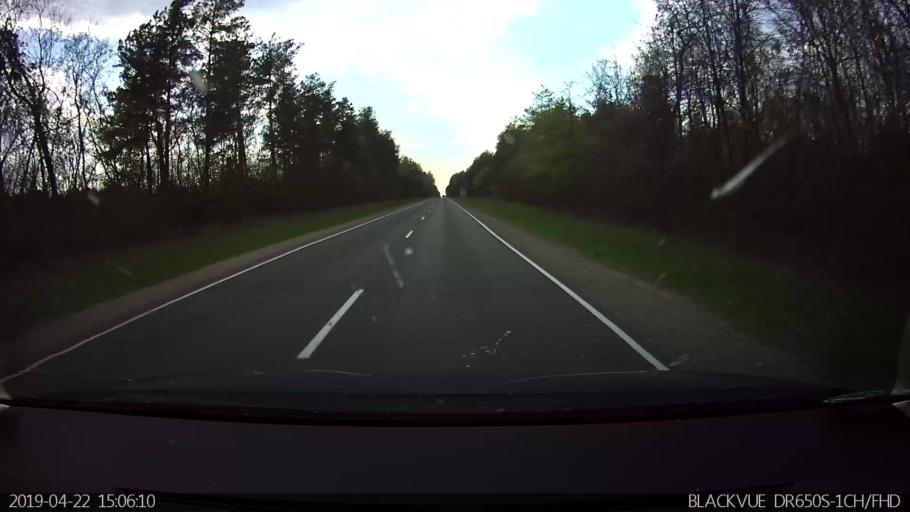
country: BY
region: Brest
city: Kamyanyets
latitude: 52.3323
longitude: 23.8452
